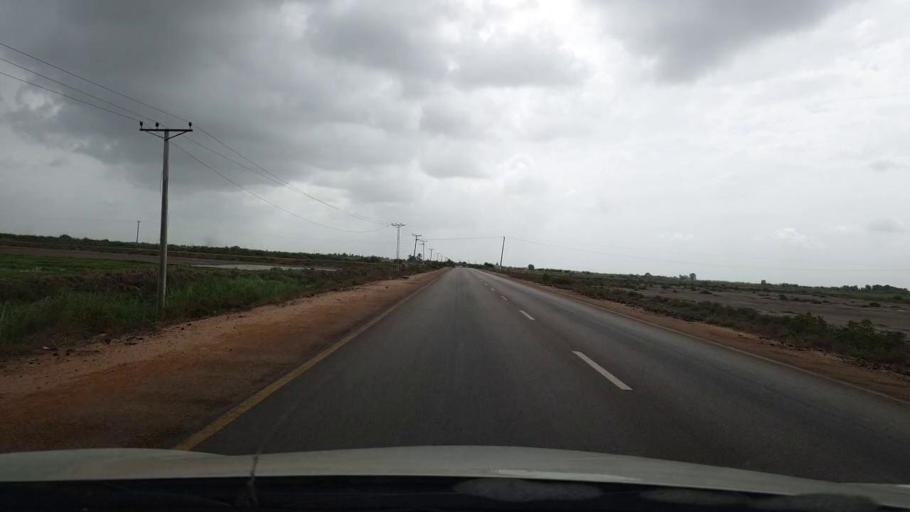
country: PK
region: Sindh
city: Mirpur Batoro
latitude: 24.5969
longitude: 68.2131
